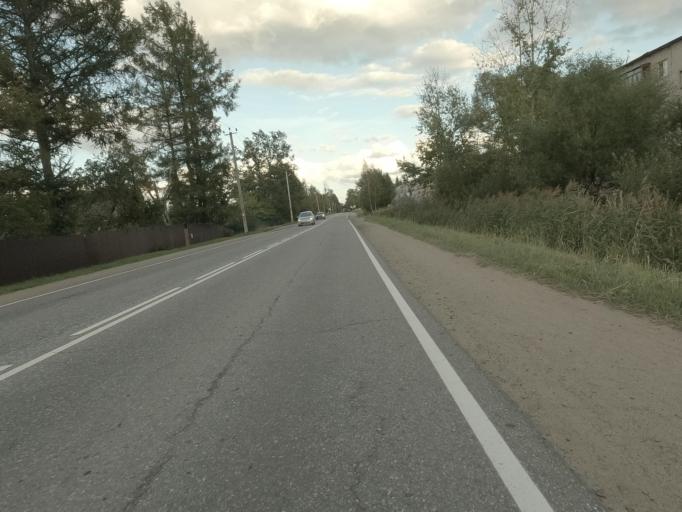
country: RU
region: Leningrad
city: Mga
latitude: 59.7529
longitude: 31.0391
